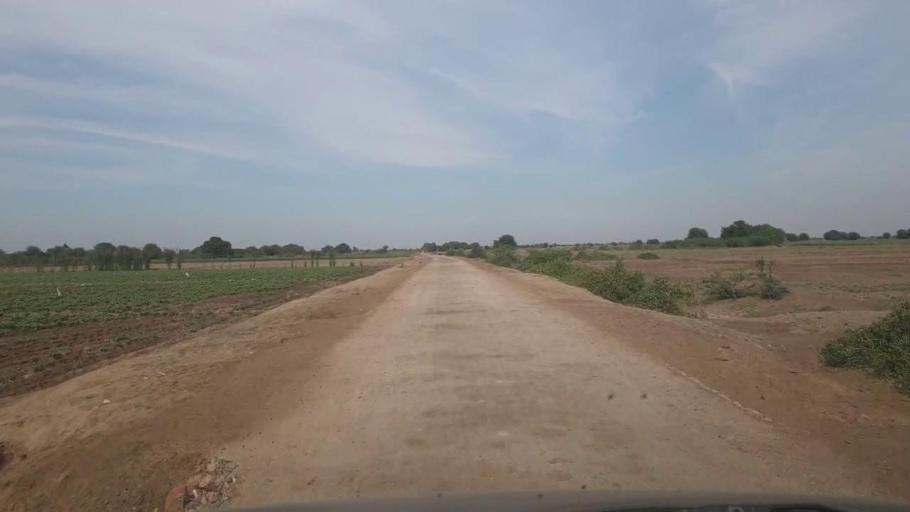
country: PK
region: Sindh
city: Kunri
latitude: 25.2687
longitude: 69.6046
